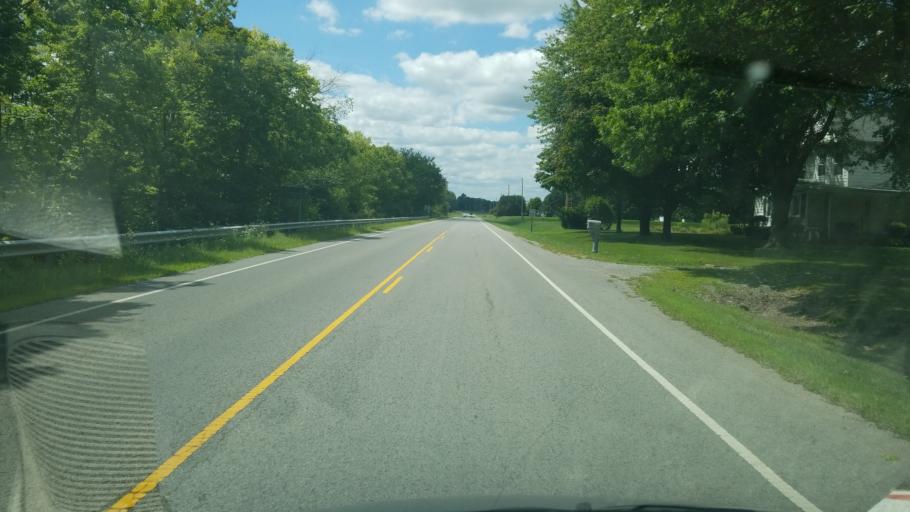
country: US
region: Ohio
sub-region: Henry County
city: Liberty Center
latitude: 41.4116
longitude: -84.0641
